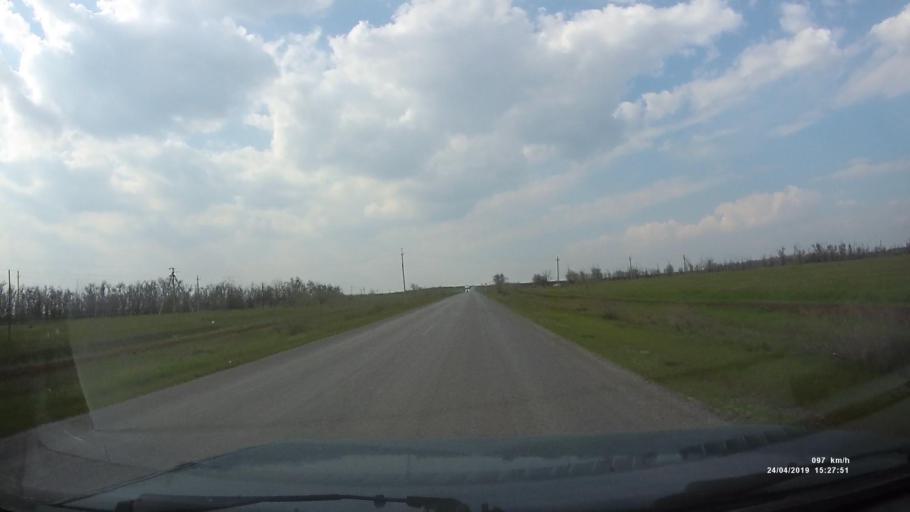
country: RU
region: Rostov
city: Remontnoye
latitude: 46.5705
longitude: 43.0229
